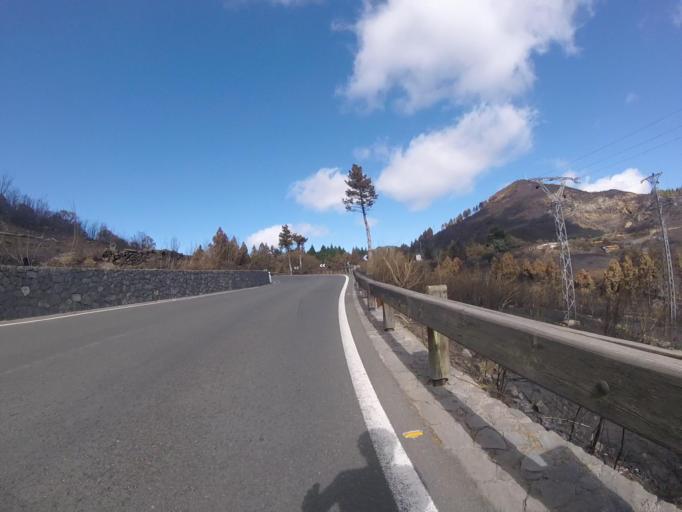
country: ES
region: Canary Islands
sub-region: Provincia de Las Palmas
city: Tejeda
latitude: 28.0052
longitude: -15.5973
